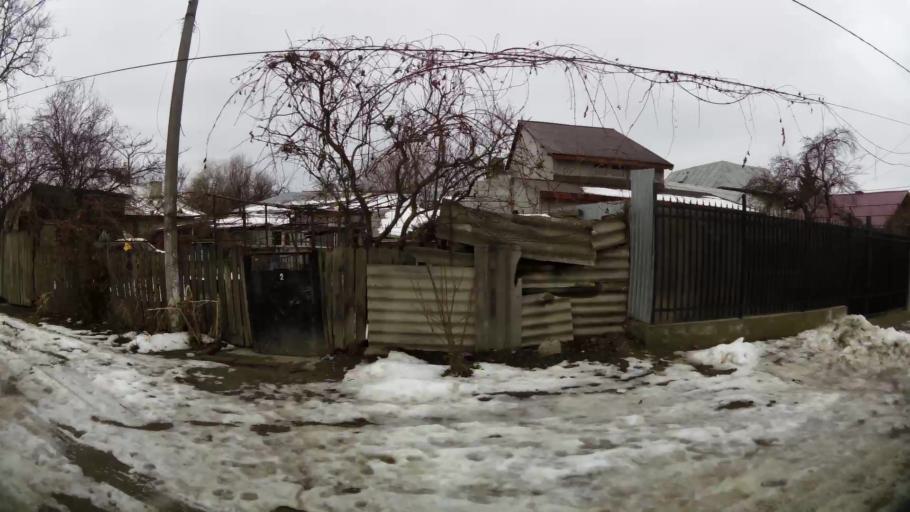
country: RO
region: Ilfov
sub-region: Comuna Pantelimon
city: Pantelimon
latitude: 44.4549
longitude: 26.1946
